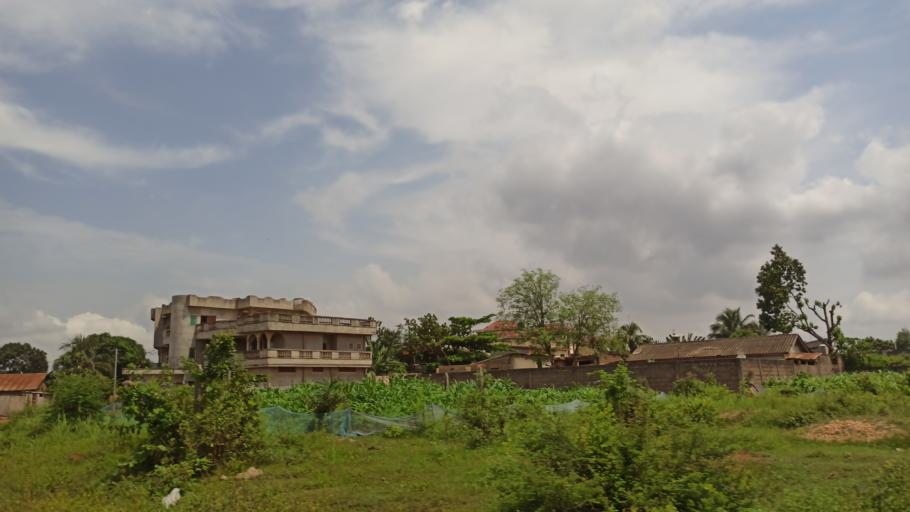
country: BJ
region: Queme
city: Porto-Novo
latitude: 6.4863
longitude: 2.5898
